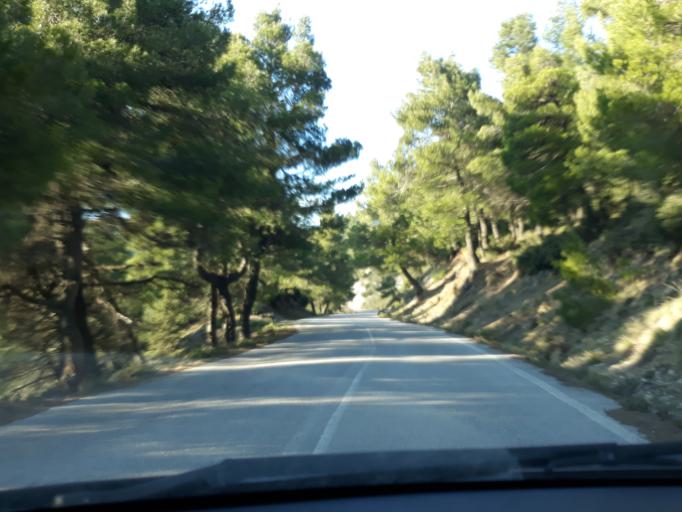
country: GR
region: Attica
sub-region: Nomarchia Dytikis Attikis
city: Fyli
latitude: 38.1494
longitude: 23.6325
